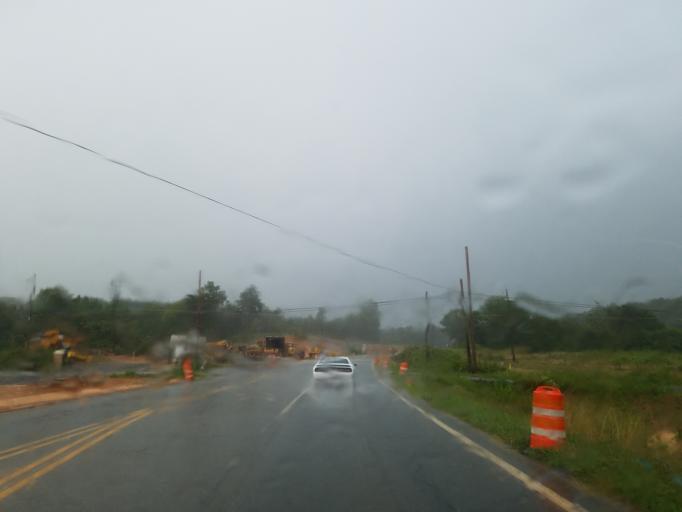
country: US
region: Georgia
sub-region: Bartow County
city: Adairsville
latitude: 34.3737
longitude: -84.9889
